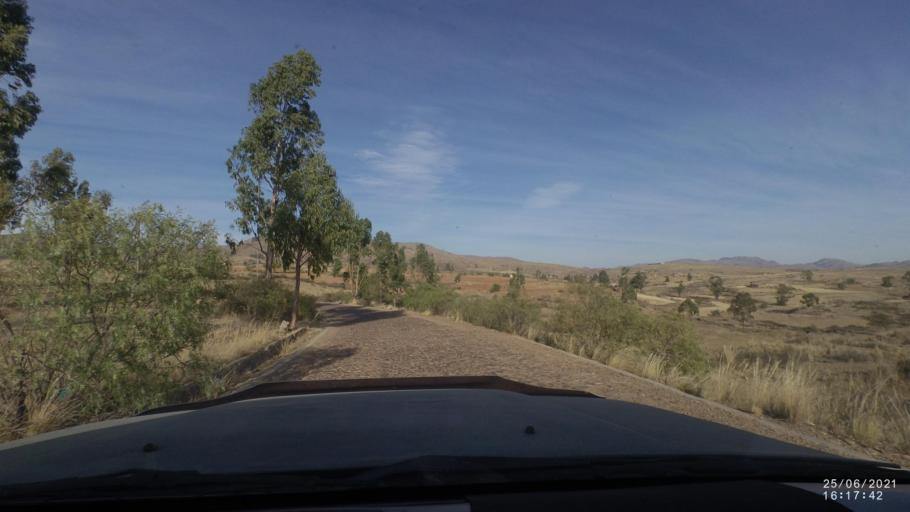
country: BO
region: Cochabamba
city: Cliza
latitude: -17.7289
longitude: -65.8544
